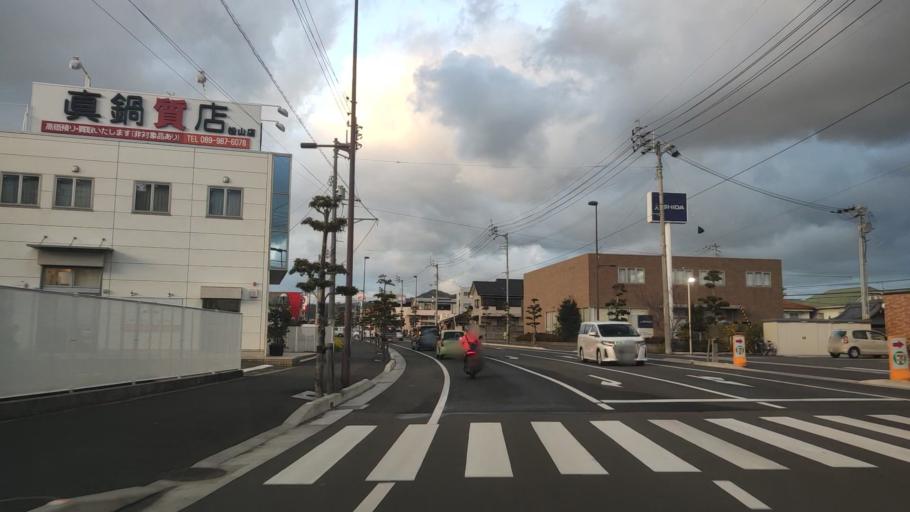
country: JP
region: Ehime
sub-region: Shikoku-chuo Shi
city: Matsuyama
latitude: 33.8298
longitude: 132.7874
